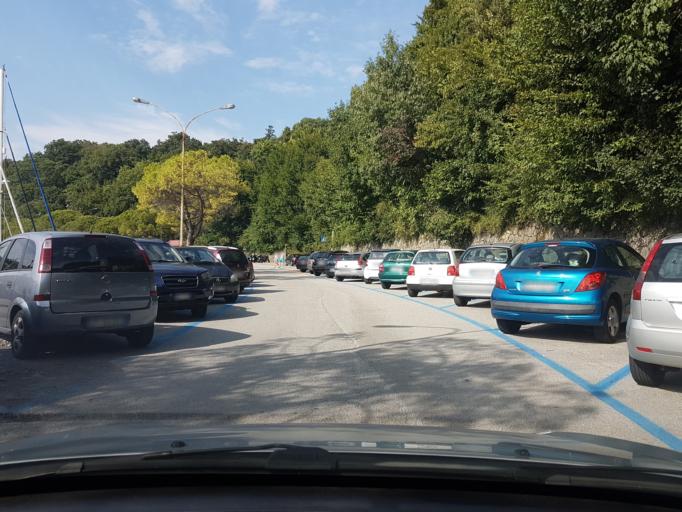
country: IT
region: Friuli Venezia Giulia
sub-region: Provincia di Trieste
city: Sistiana-Visogliano
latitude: 45.7687
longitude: 13.6328
